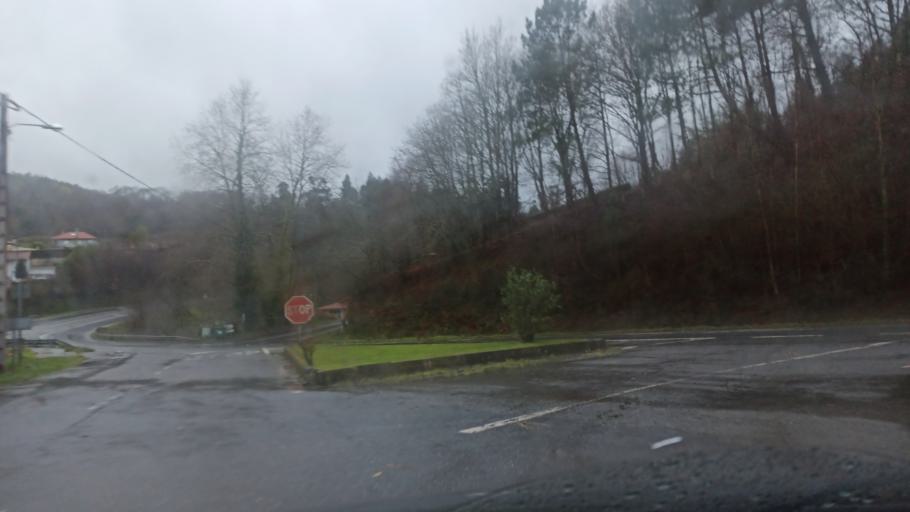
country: ES
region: Galicia
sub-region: Provincia da Coruna
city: Cesuras
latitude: 43.1757
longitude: -8.1755
